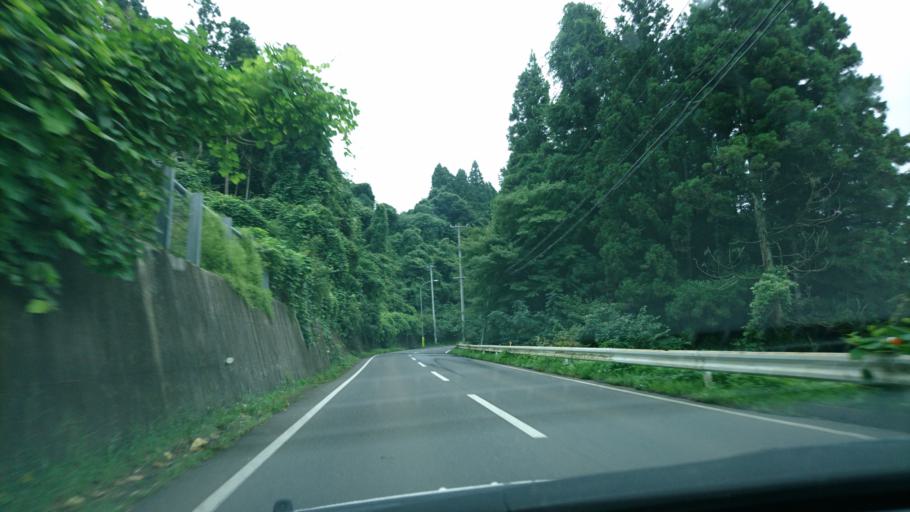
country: JP
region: Iwate
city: Ichinoseki
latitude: 38.9106
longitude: 141.0647
